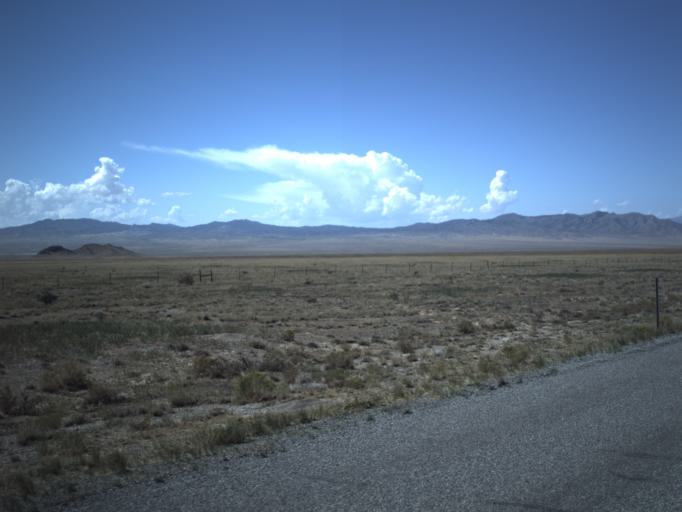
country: US
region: Utah
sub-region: Beaver County
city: Milford
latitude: 39.0649
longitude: -113.7435
